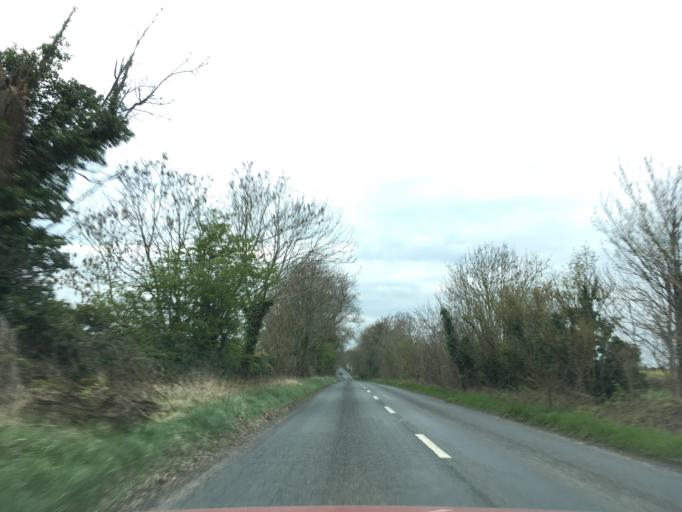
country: GB
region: England
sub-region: Gloucestershire
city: Bourton on the Water
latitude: 51.7890
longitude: -1.7302
